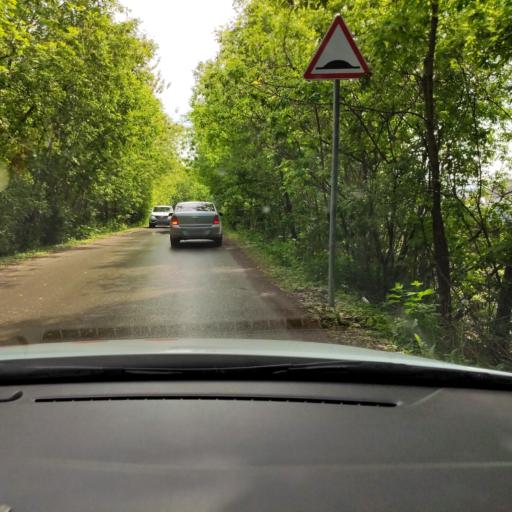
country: RU
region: Tatarstan
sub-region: Gorod Kazan'
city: Kazan
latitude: 55.7019
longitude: 49.0869
